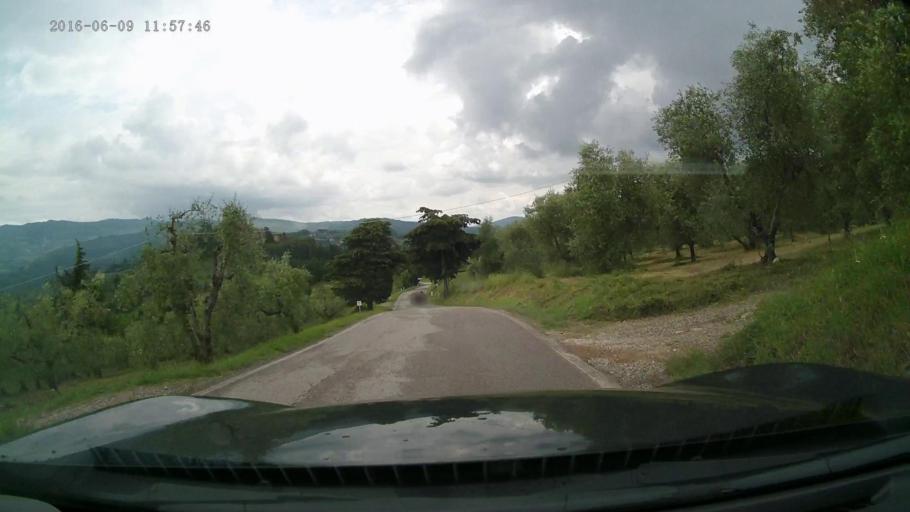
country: IT
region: Tuscany
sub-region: Province of Florence
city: Panzano in Chianti
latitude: 43.5510
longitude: 11.3034
